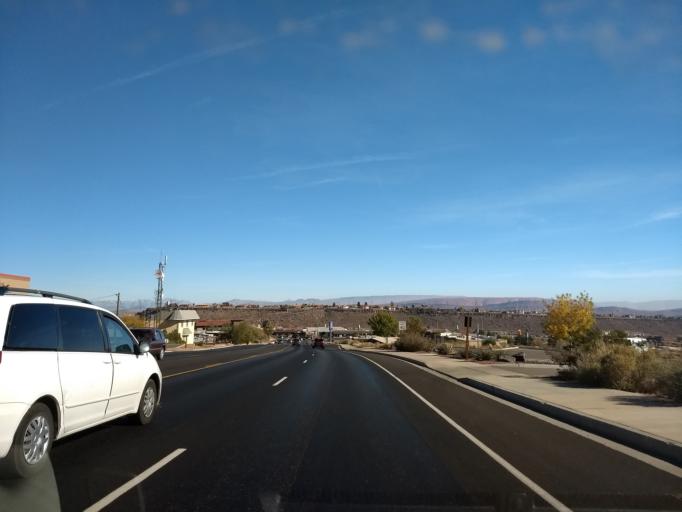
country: US
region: Utah
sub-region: Washington County
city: Saint George
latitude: 37.1122
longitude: -113.5667
